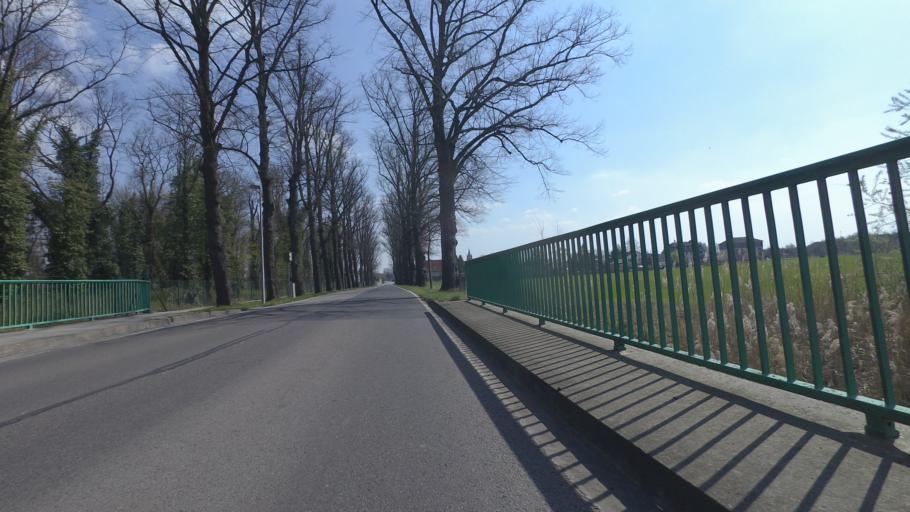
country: DE
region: Brandenburg
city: Mittenwalde
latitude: 52.2696
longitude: 13.5265
